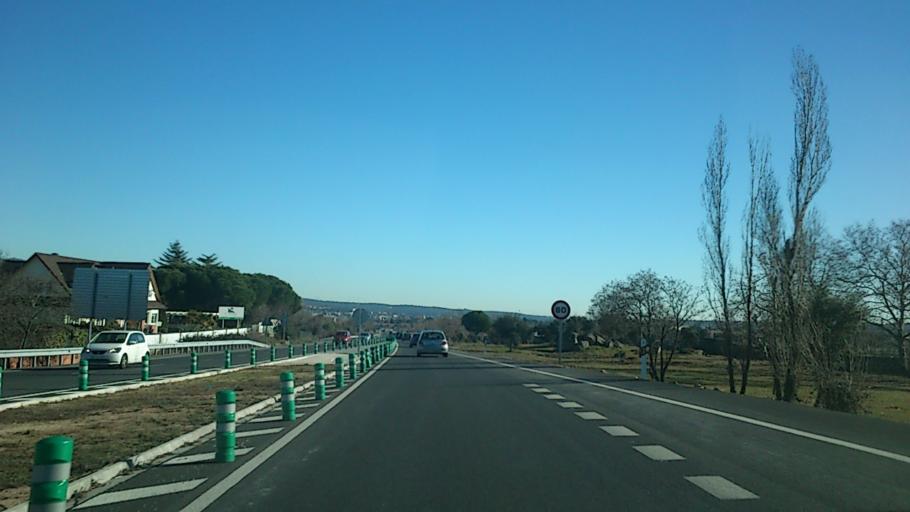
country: ES
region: Madrid
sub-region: Provincia de Madrid
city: Alpedrete
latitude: 40.6486
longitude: -4.0464
